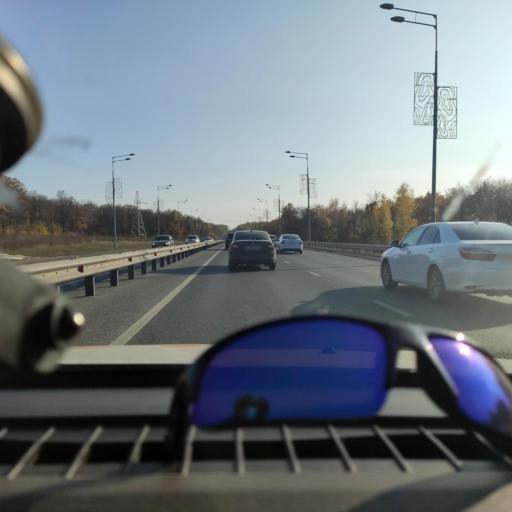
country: RU
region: Samara
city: Novosemeykino
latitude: 53.3372
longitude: 50.2320
